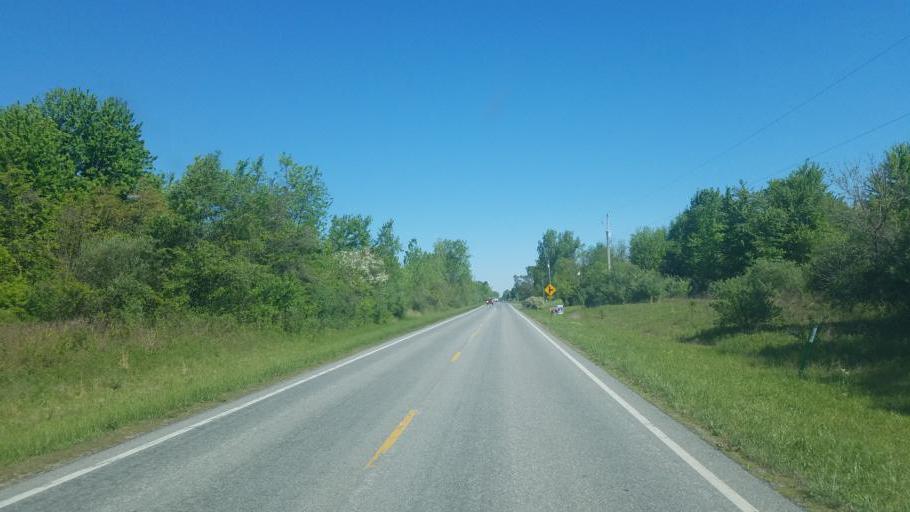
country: US
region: Ohio
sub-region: Delaware County
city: Lewis Center
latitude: 40.2080
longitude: -82.9489
